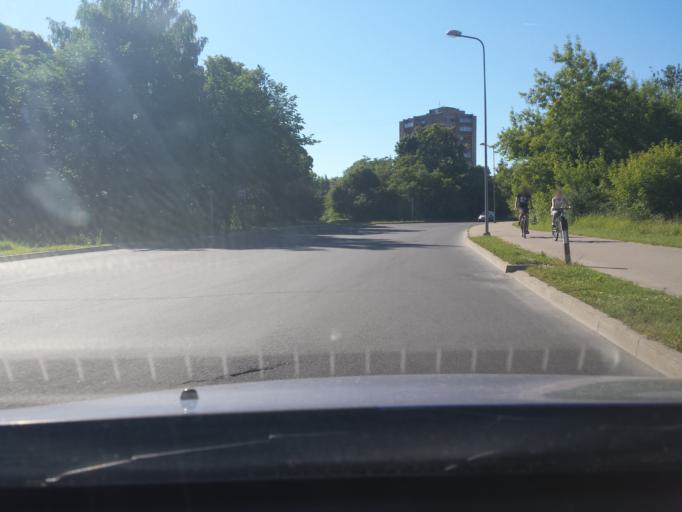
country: LV
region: Riga
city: Jaunciems
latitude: 56.9945
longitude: 24.1738
